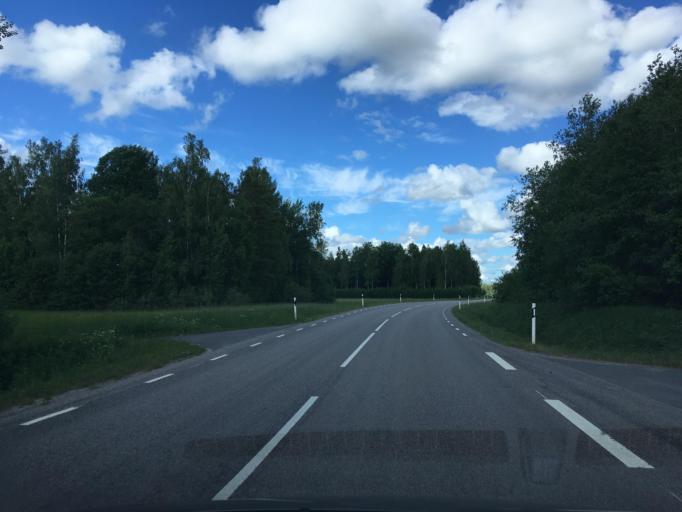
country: EE
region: Paernumaa
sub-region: Halinga vald
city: Parnu-Jaagupi
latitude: 58.6651
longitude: 24.5810
